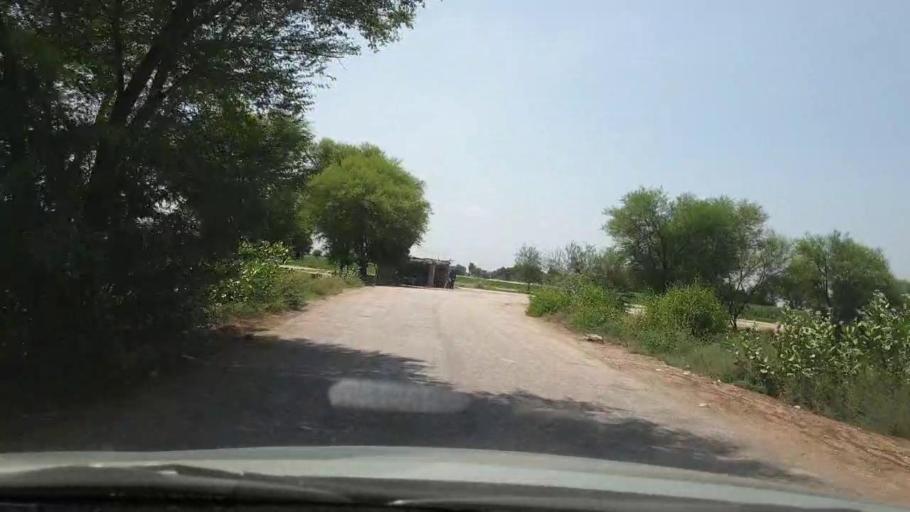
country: PK
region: Sindh
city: Pano Aqil
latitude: 27.6636
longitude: 69.1084
